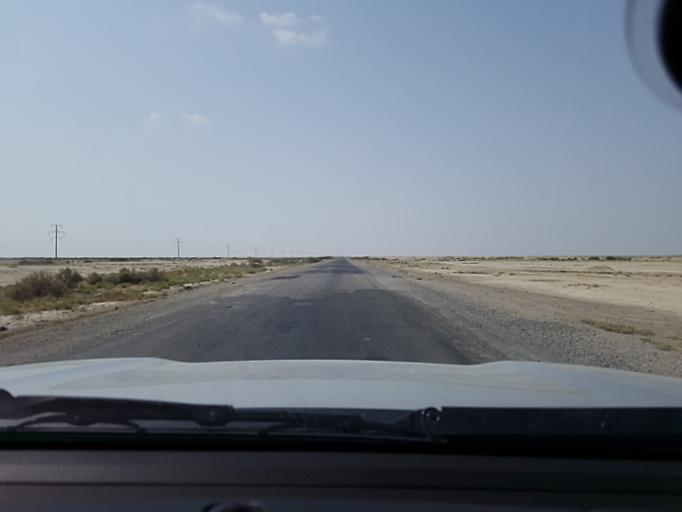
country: TM
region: Balkan
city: Gumdag
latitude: 38.9017
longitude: 54.5923
